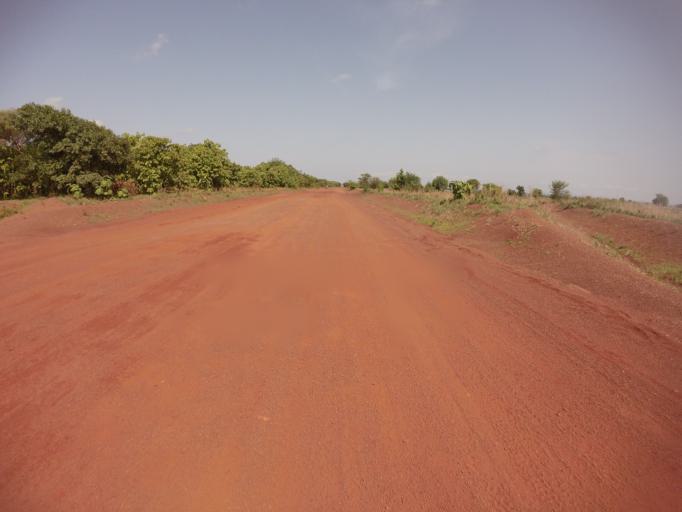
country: GH
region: Upper East
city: Bawku
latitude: 11.0014
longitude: -0.1961
